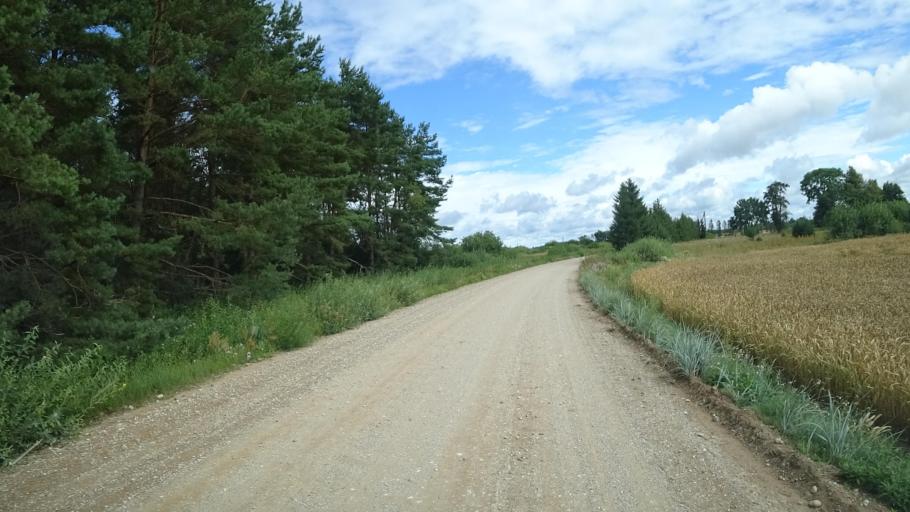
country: LV
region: Liepaja
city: Vec-Liepaja
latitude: 56.6483
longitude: 21.0449
